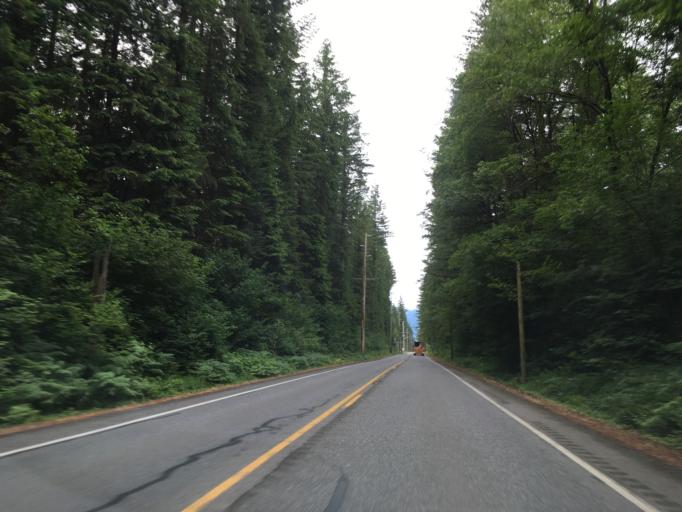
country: US
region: Washington
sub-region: Whatcom County
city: Peaceful Valley
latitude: 48.9636
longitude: -122.1610
